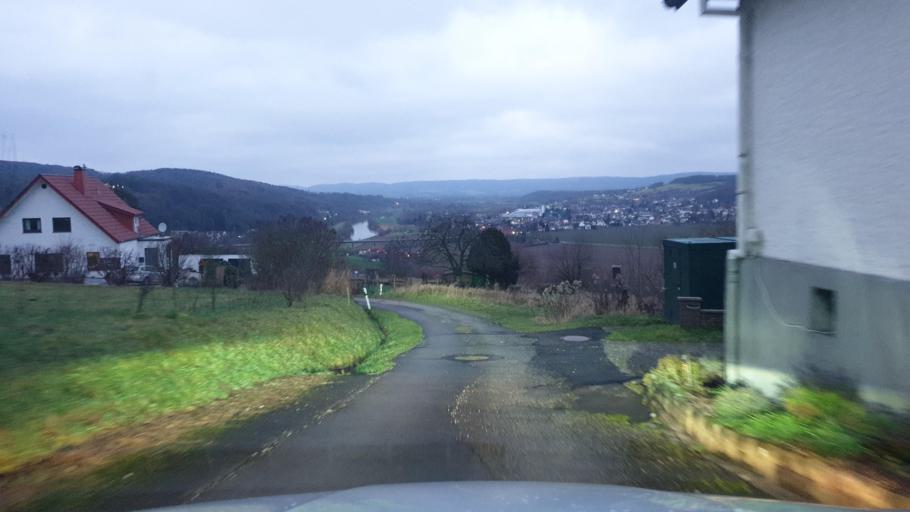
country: DE
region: North Rhine-Westphalia
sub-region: Regierungsbezirk Detmold
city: Vlotho
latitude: 52.1624
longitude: 8.8744
